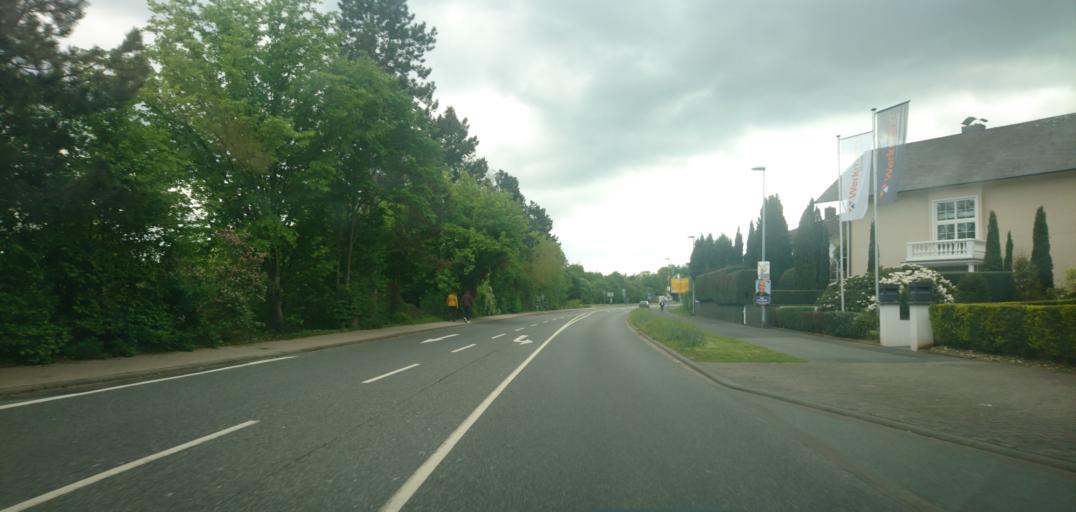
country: DE
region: Hesse
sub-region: Regierungsbezirk Darmstadt
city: Dietzenbach
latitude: 50.0034
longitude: 8.7744
